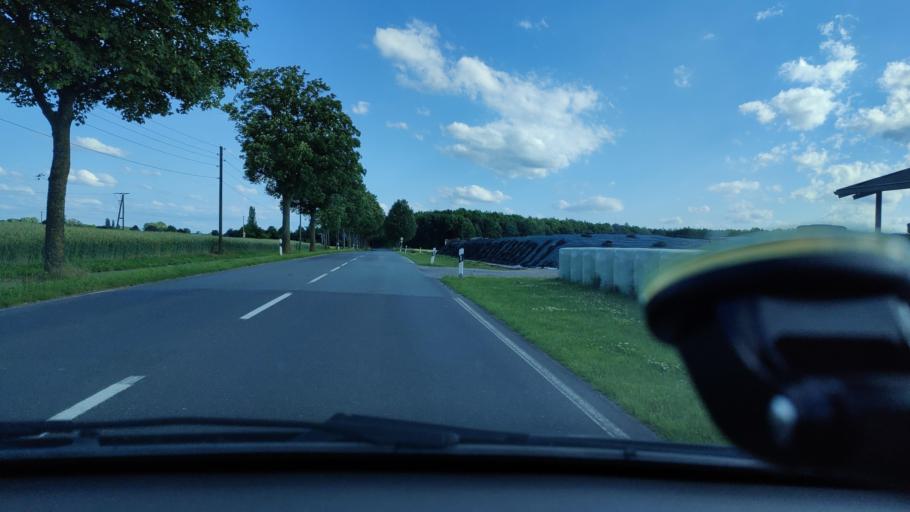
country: DE
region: North Rhine-Westphalia
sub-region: Regierungsbezirk Dusseldorf
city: Alpen
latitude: 51.5503
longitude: 6.5314
